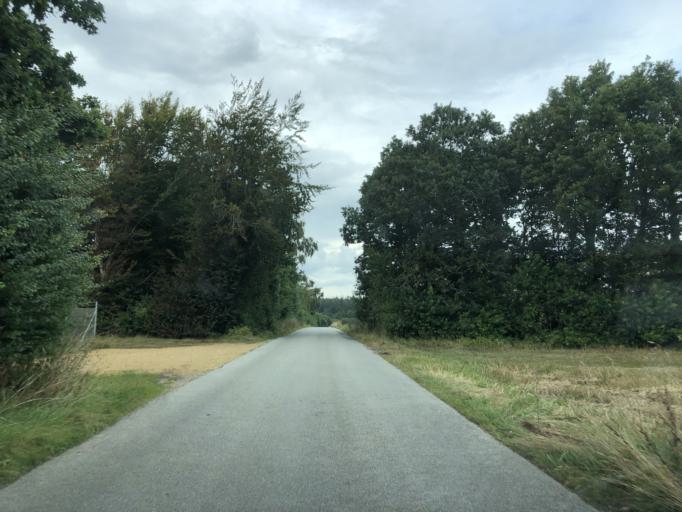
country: DK
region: Central Jutland
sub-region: Holstebro Kommune
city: Ulfborg
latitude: 56.1973
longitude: 8.4236
